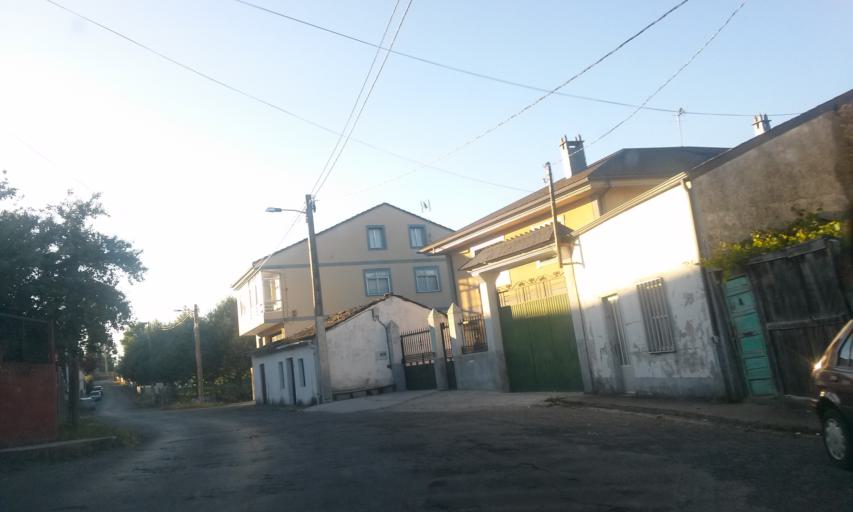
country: ES
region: Galicia
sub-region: Provincia de Lugo
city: Lugo
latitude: 43.0272
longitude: -7.5598
